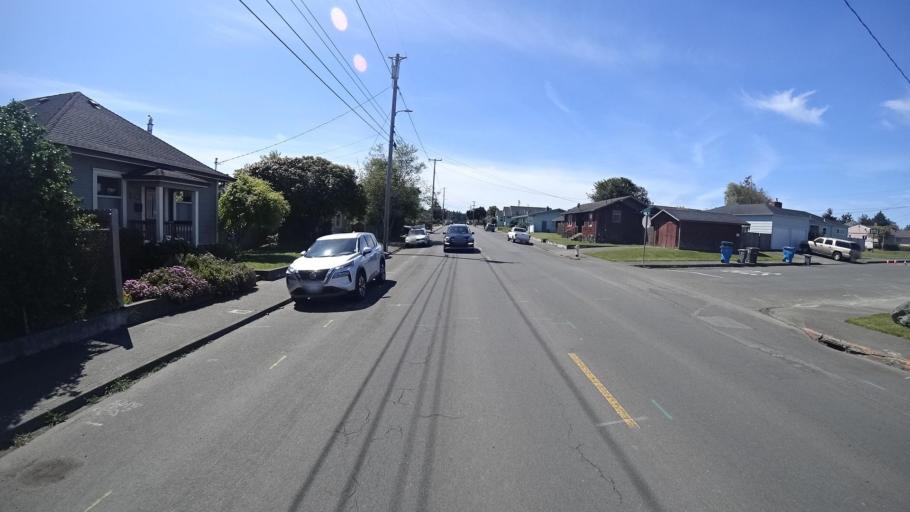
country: US
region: California
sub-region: Humboldt County
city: Eureka
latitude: 40.7961
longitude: -124.1481
